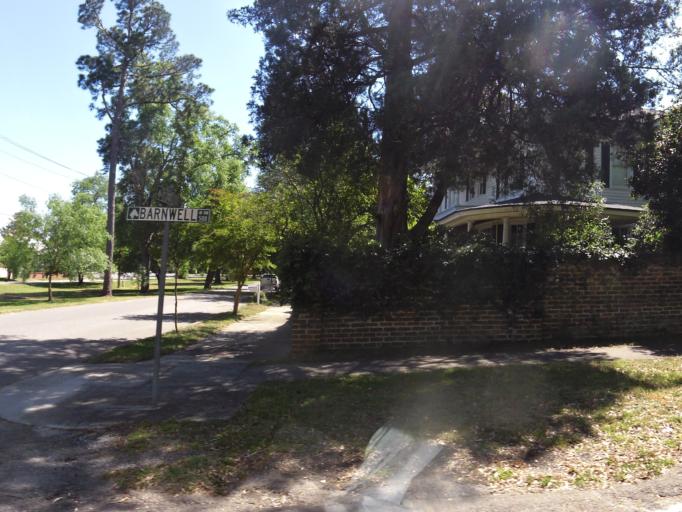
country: US
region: South Carolina
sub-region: Aiken County
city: Aiken
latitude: 33.5644
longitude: -81.7246
